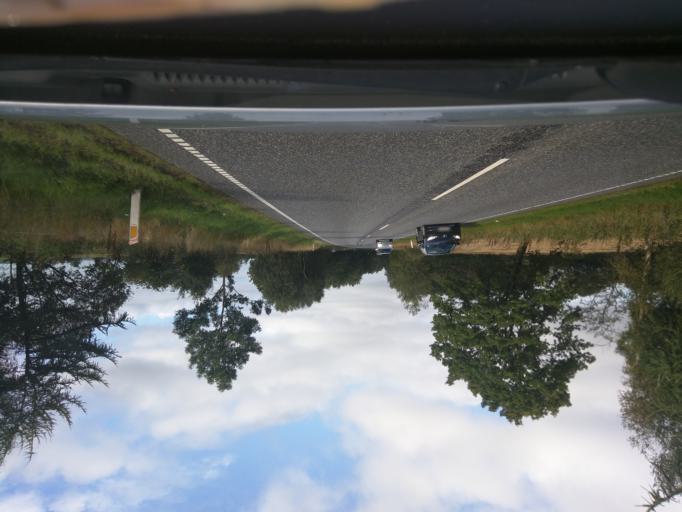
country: DK
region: Central Jutland
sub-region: Viborg Kommune
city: Viborg
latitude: 56.3825
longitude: 9.3805
